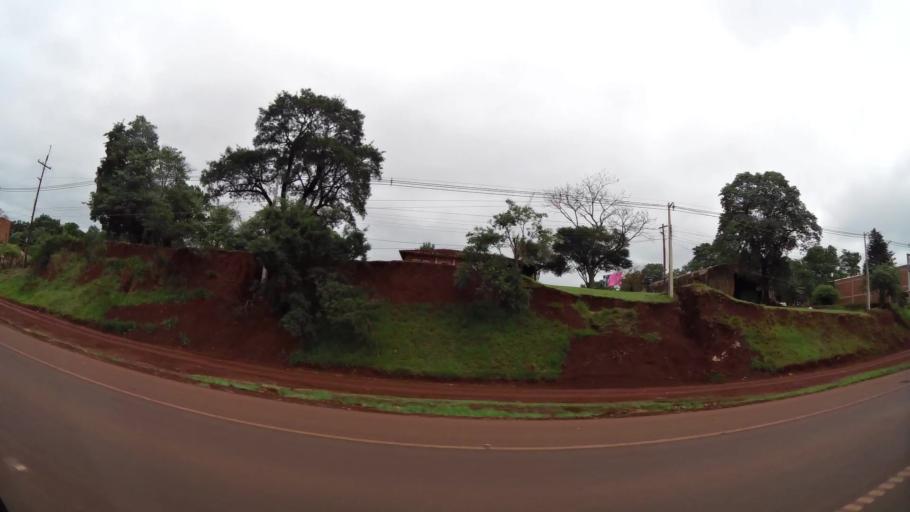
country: PY
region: Alto Parana
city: Presidente Franco
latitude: -25.4904
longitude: -54.7762
